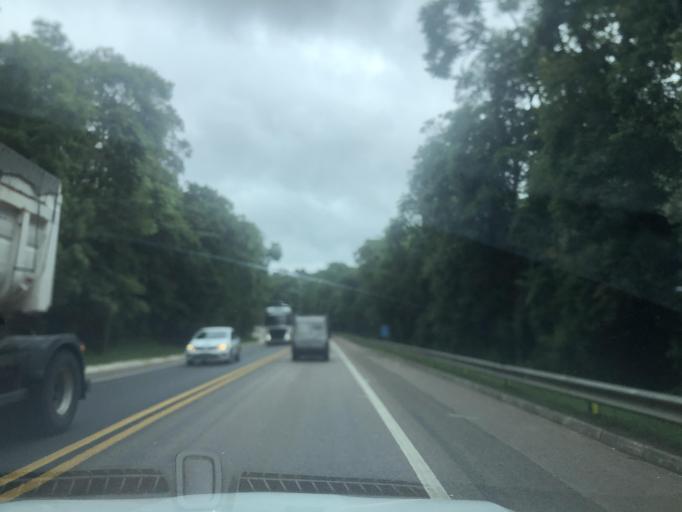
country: BR
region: Parana
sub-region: Araucaria
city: Araucaria
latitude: -25.8499
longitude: -49.3565
